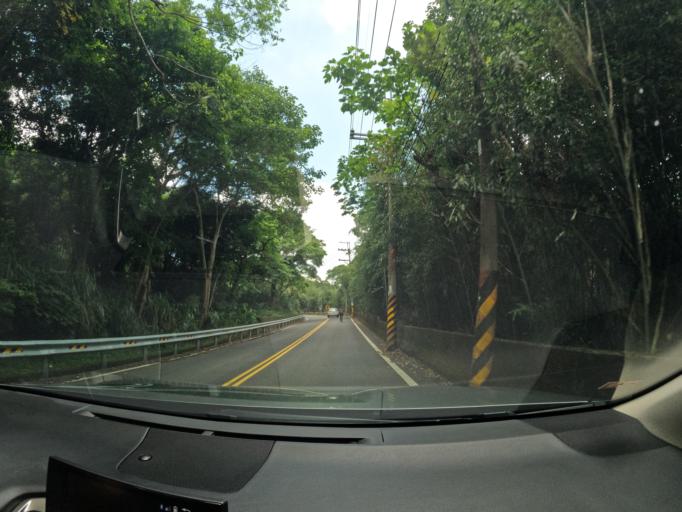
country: TW
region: Taiwan
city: Fengyuan
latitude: 24.3849
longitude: 120.8138
